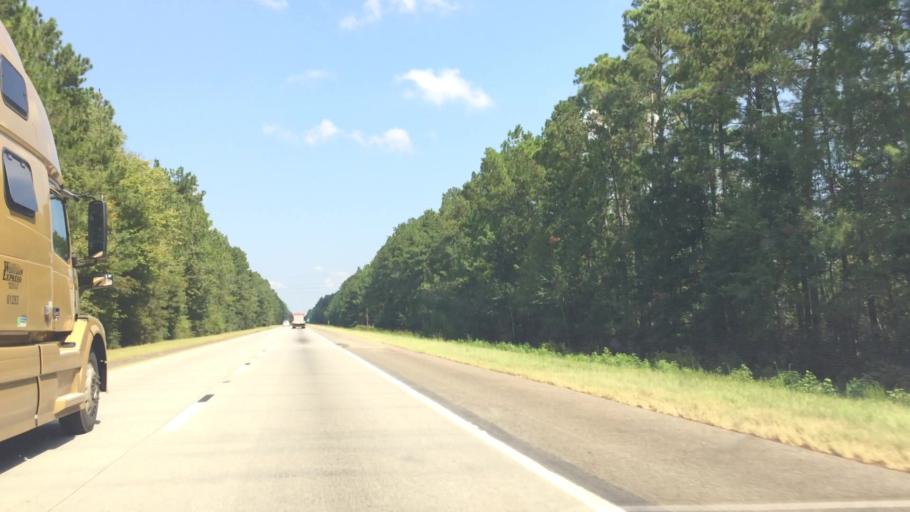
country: US
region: South Carolina
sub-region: Colleton County
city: Walterboro
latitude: 33.0575
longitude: -80.6645
